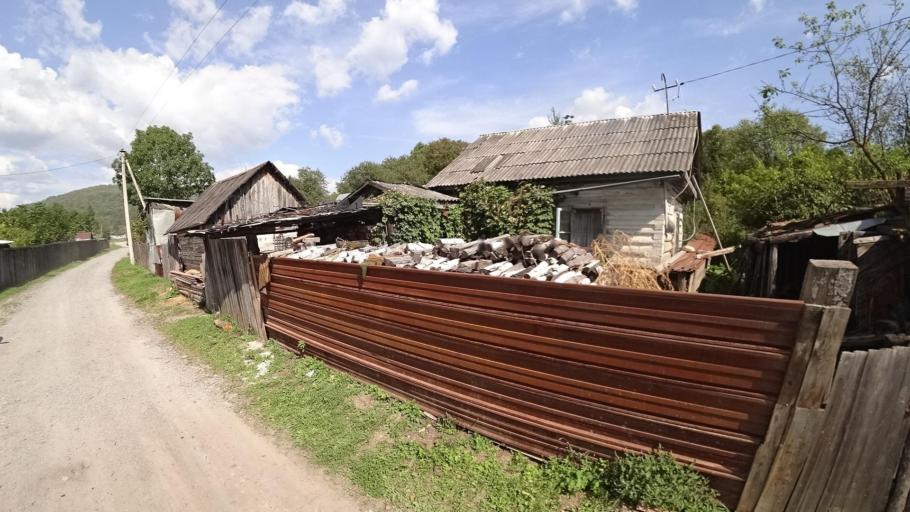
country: RU
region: Jewish Autonomous Oblast
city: Londoko
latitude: 49.0248
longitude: 131.9325
